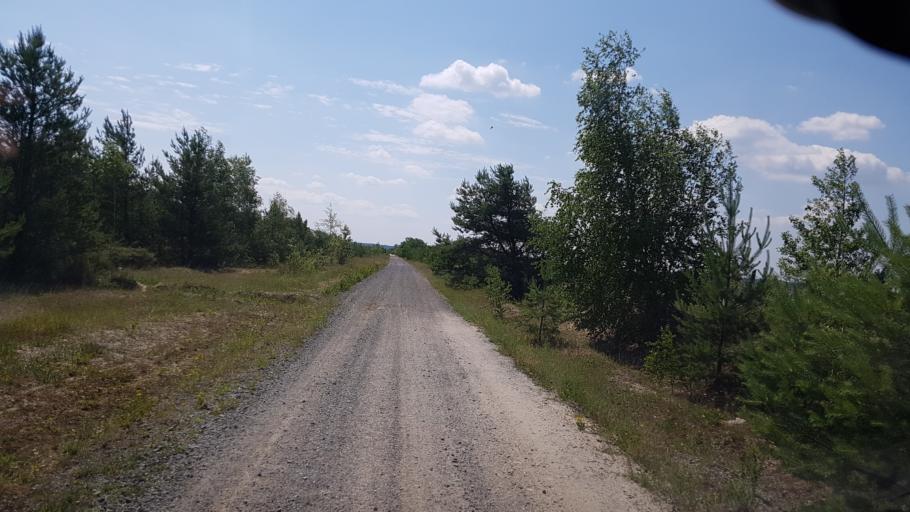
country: DE
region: Brandenburg
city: Sallgast
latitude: 51.5761
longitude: 13.8020
